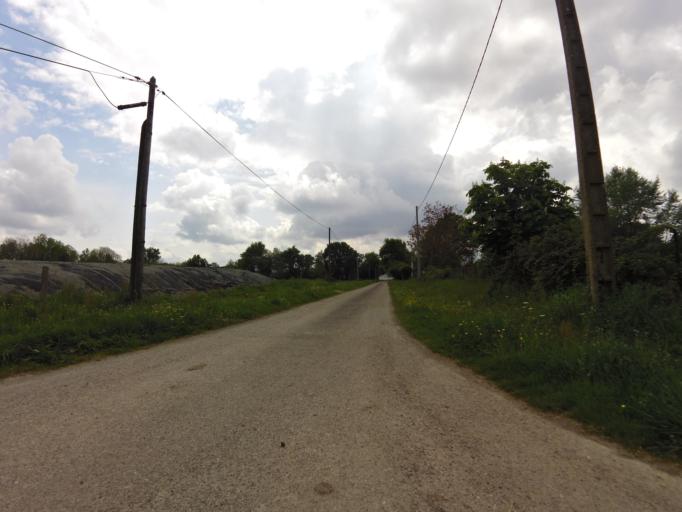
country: FR
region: Brittany
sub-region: Departement du Morbihan
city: Saint-Martin-sur-Oust
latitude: 47.7292
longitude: -2.2747
